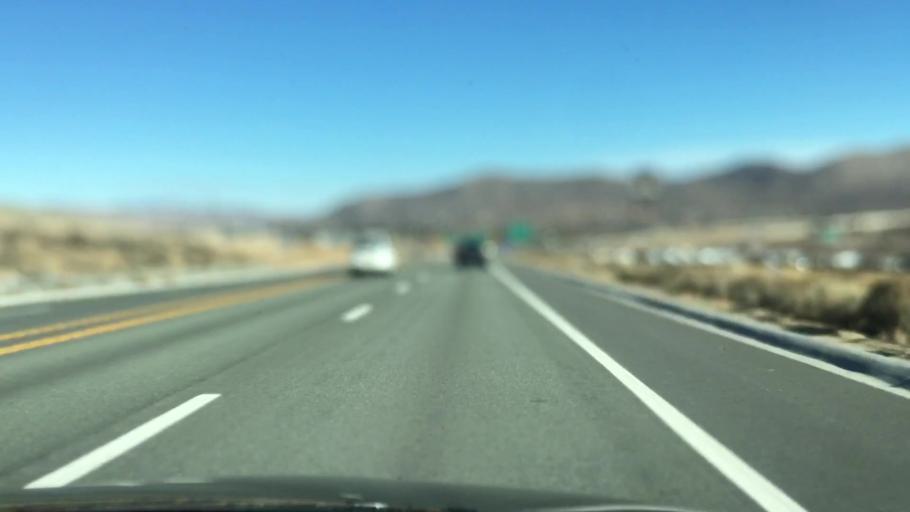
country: US
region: Nevada
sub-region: Douglas County
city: Indian Hills
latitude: 39.1169
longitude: -119.7796
